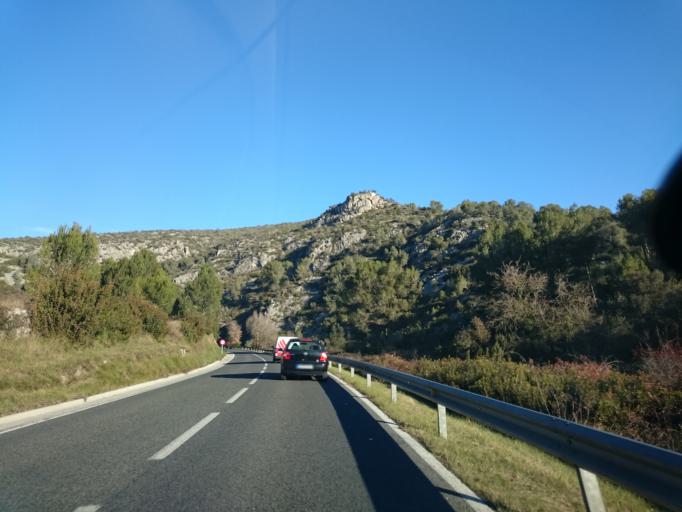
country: ES
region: Catalonia
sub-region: Provincia de Barcelona
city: Sant Pere de Ribes
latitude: 41.2887
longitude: 1.7373
